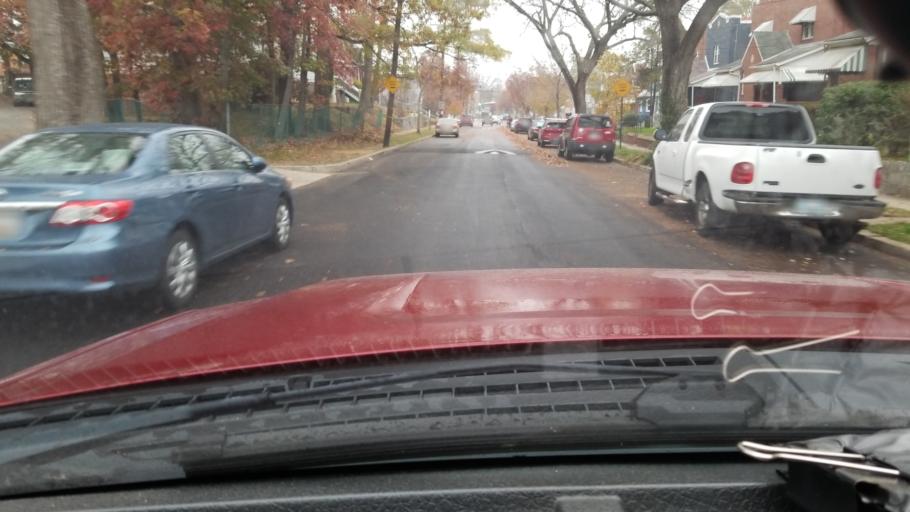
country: US
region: Maryland
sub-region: Prince George's County
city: Capitol Heights
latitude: 38.8881
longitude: -76.9257
